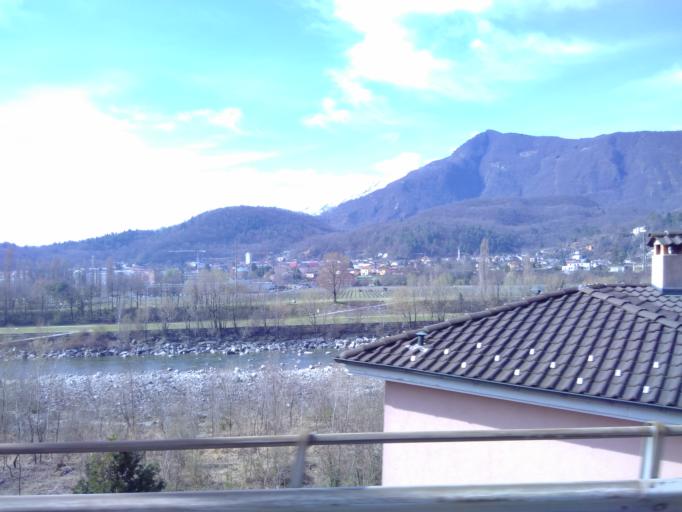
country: CH
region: Ticino
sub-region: Locarno District
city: Losone
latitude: 46.1728
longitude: 8.7690
